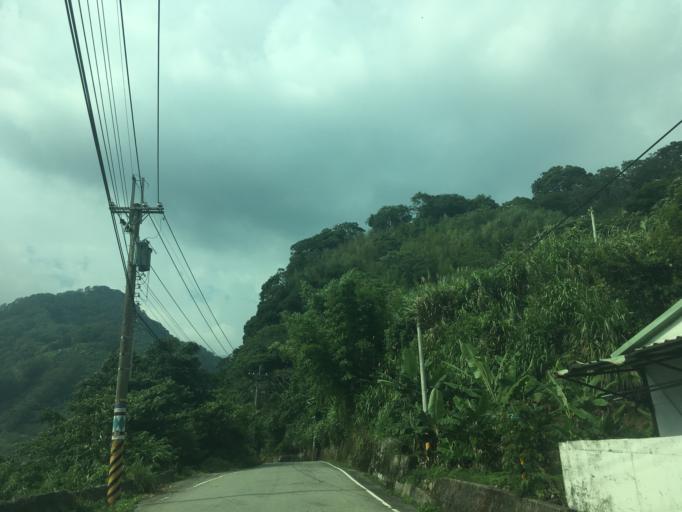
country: TW
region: Taiwan
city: Fengyuan
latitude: 24.3408
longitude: 120.9358
